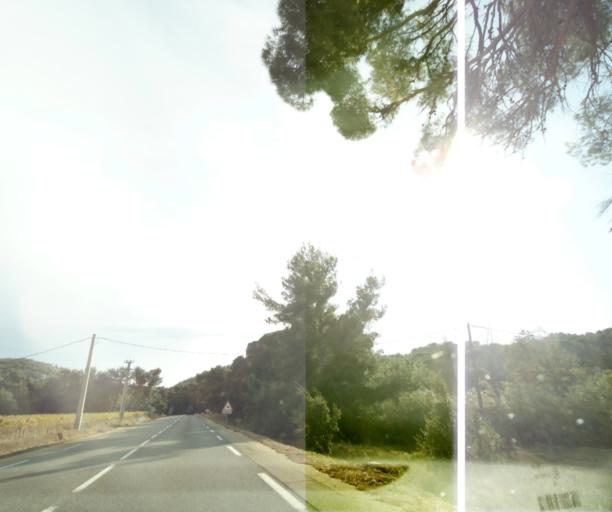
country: FR
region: Provence-Alpes-Cote d'Azur
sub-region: Departement des Bouches-du-Rhone
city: Sausset-les-Pins
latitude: 43.3587
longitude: 5.1018
